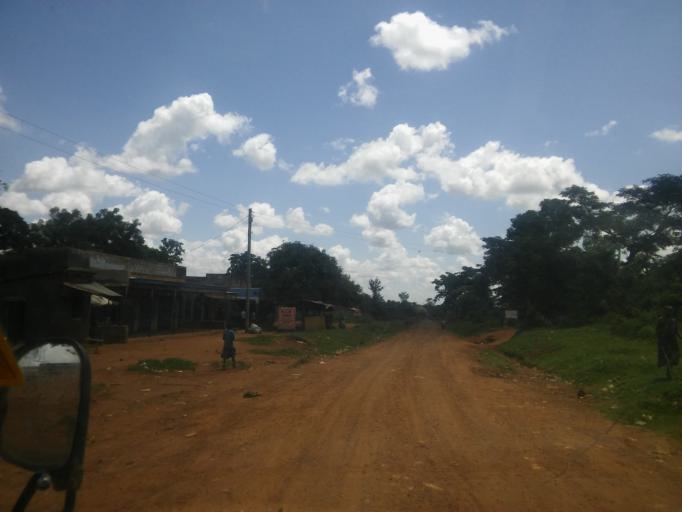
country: UG
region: Eastern Region
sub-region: Budaka District
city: Budaka
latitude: 1.1087
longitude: 33.9680
